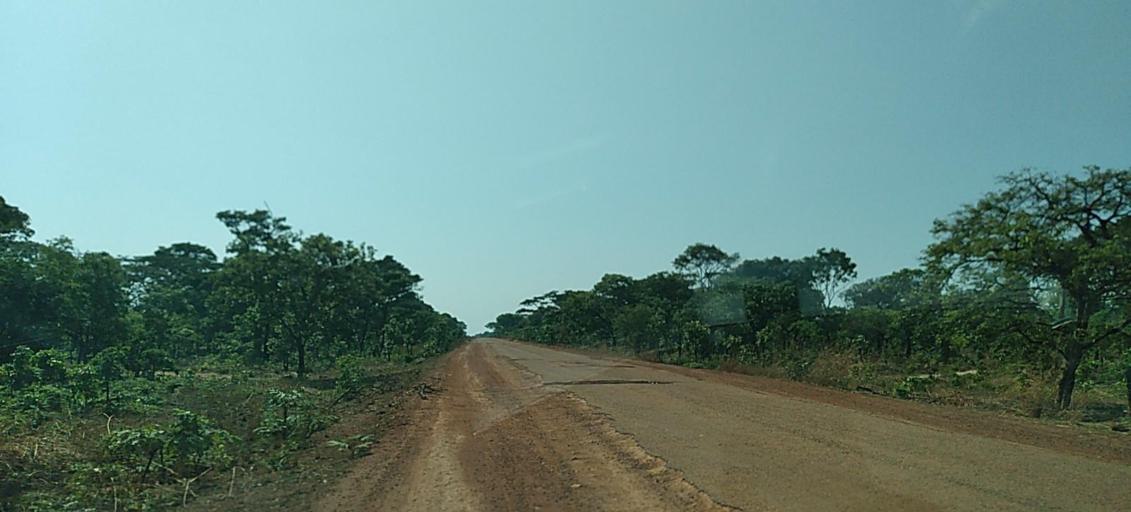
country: ZM
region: North-Western
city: Mwinilunga
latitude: -11.9084
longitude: 25.2934
